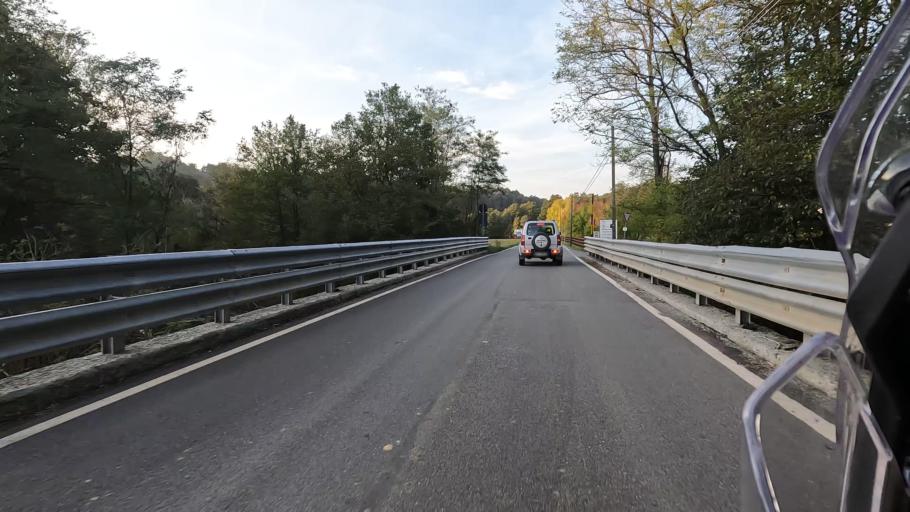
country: IT
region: Liguria
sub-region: Provincia di Savona
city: Sassello
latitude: 44.5033
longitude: 8.4839
